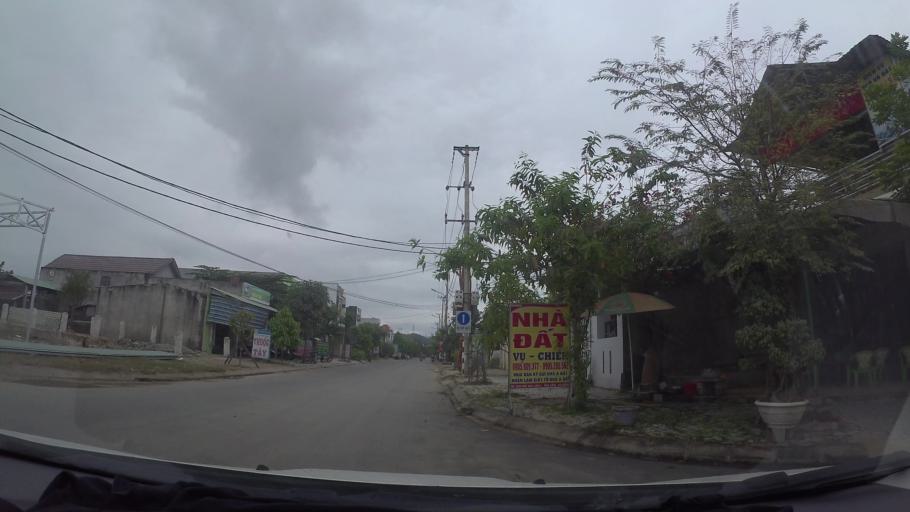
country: VN
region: Da Nang
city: Lien Chieu
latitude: 16.0938
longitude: 108.1043
